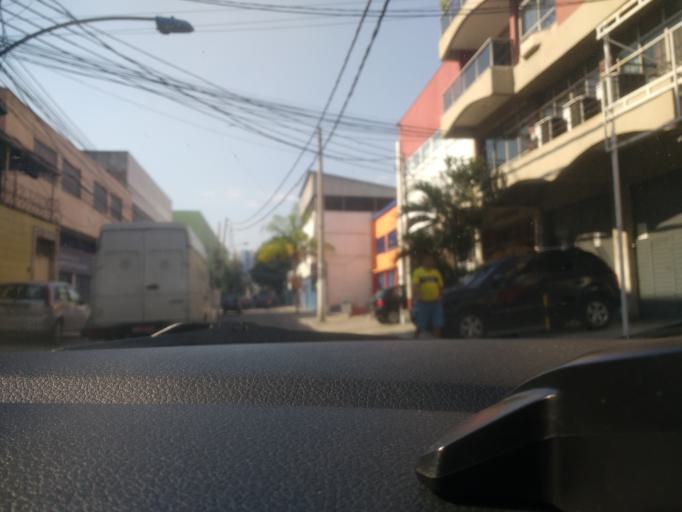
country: BR
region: Rio de Janeiro
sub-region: Duque De Caxias
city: Duque de Caxias
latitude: -22.7932
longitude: -43.3019
